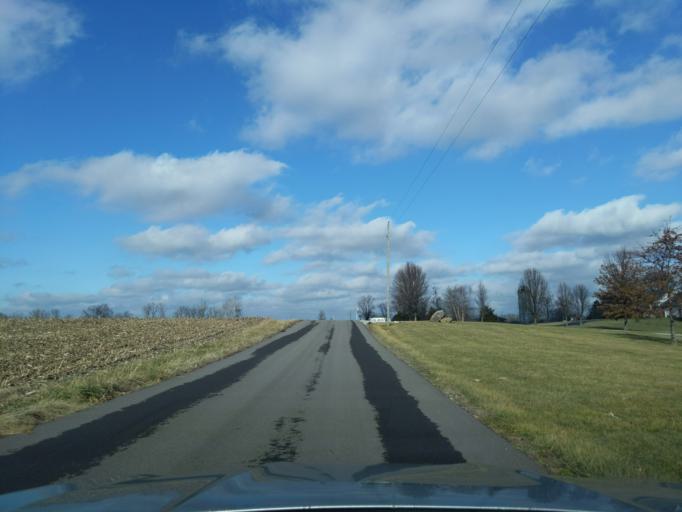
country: US
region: Indiana
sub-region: Decatur County
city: Greensburg
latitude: 39.2648
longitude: -85.4839
